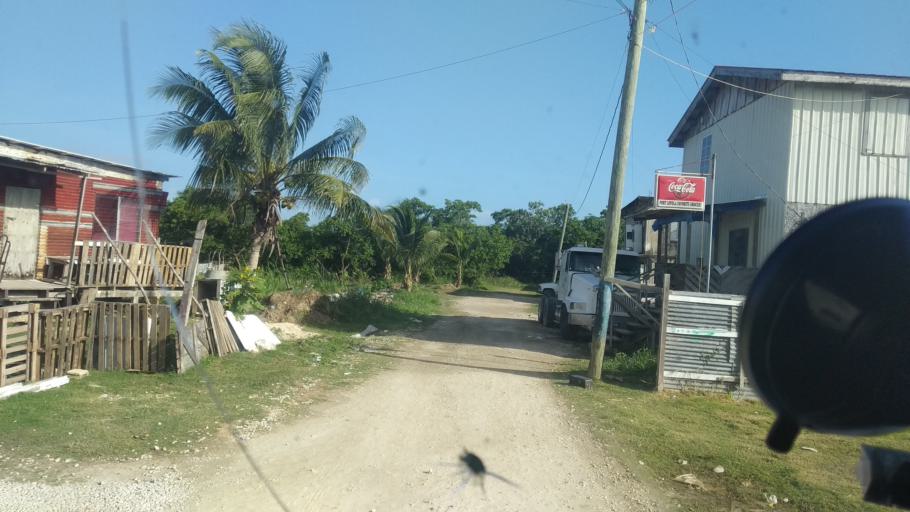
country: BZ
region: Belize
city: Belize City
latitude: 17.4852
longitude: -88.2029
